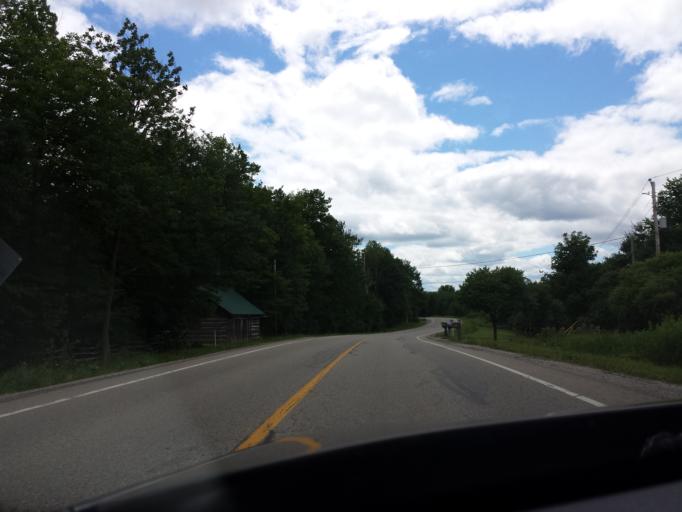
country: CA
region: Ontario
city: Perth
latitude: 44.8564
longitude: -76.1958
